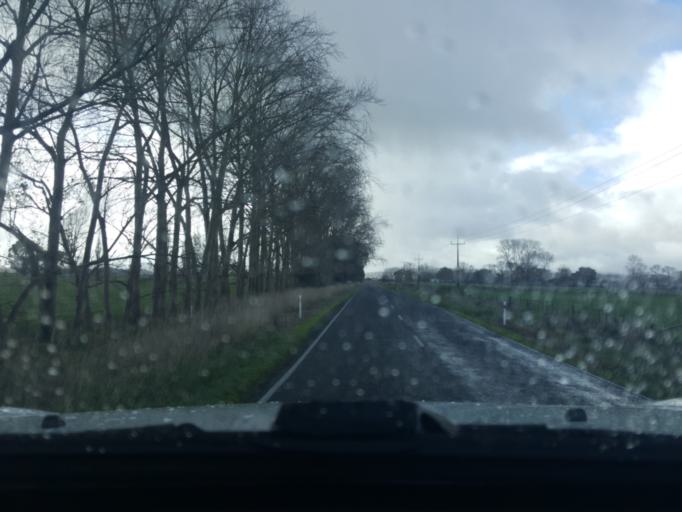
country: NZ
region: Waikato
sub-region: Waikato District
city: Te Kauwhata
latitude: -37.4469
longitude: 175.1105
